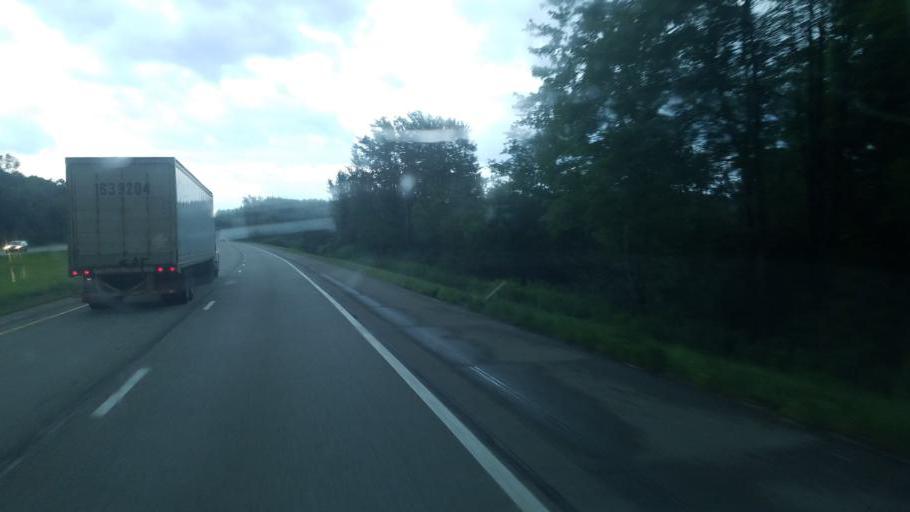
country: US
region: Pennsylvania
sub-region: Mercer County
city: Grove City
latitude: 41.0889
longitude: -80.1382
